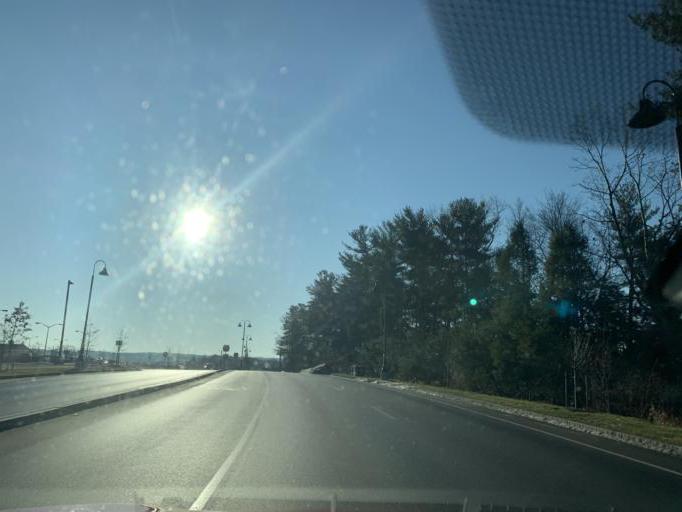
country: US
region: New Hampshire
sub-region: Rockingham County
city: Londonderry
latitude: 42.8699
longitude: -71.3497
